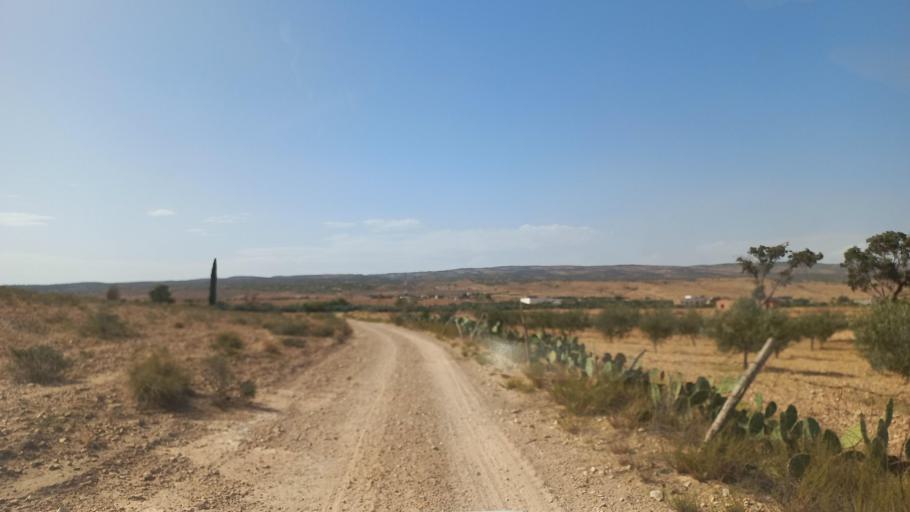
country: TN
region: Al Qasrayn
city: Kasserine
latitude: 35.2810
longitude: 8.9363
